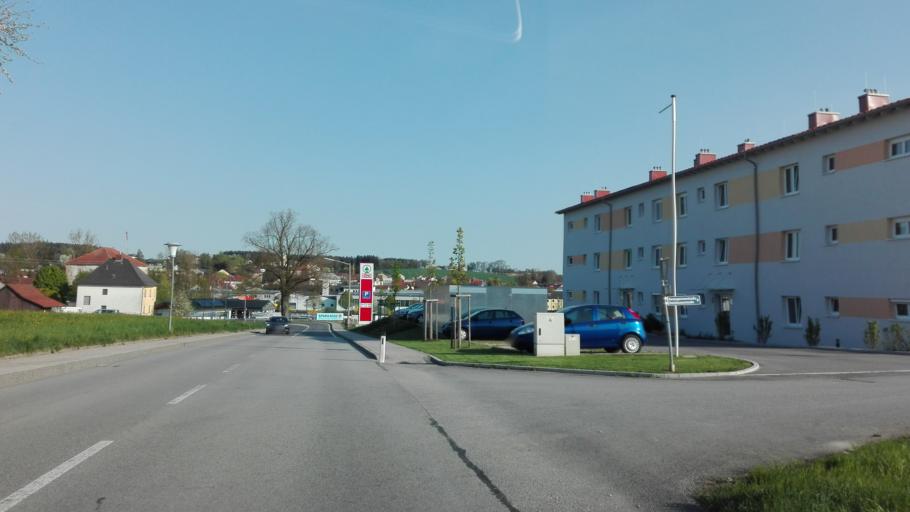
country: AT
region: Upper Austria
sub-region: Politischer Bezirk Grieskirchen
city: Grieskirchen
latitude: 48.3342
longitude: 13.8492
